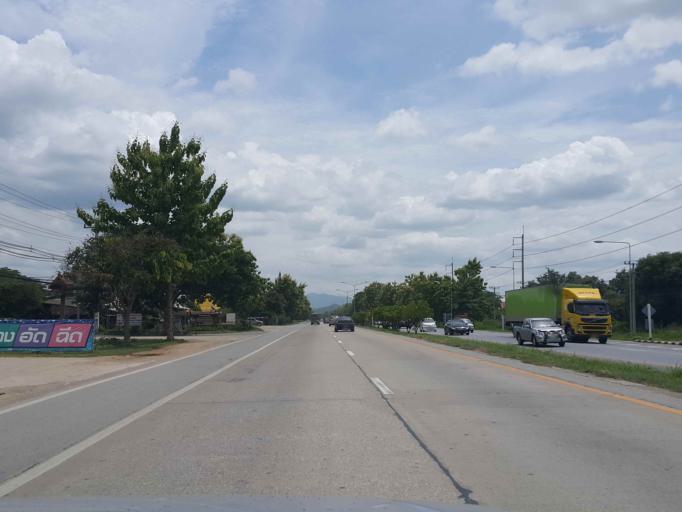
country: TH
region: Lamphun
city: Lamphun
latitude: 18.5698
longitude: 99.0444
